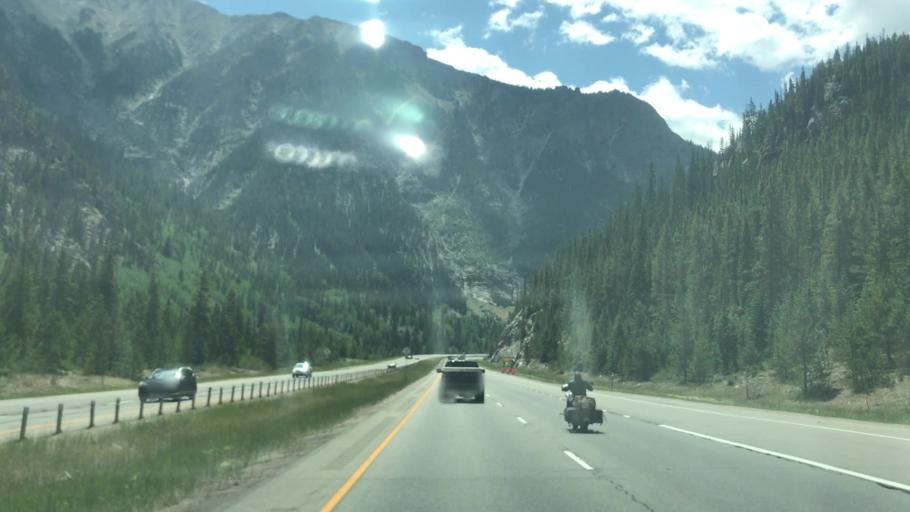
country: US
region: Colorado
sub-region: Summit County
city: Frisco
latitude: 39.5342
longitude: -106.1420
